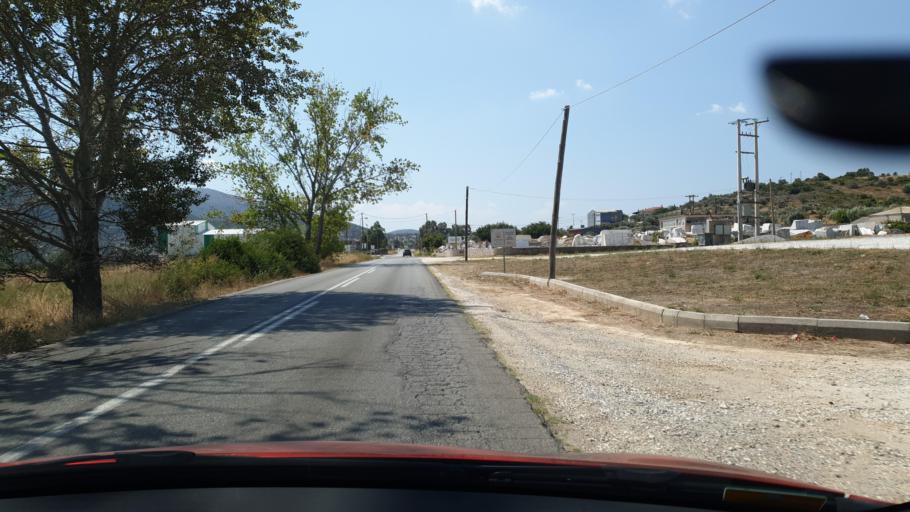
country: GR
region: Central Greece
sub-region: Nomos Evvoias
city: Aliveri
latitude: 38.3977
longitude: 24.1027
